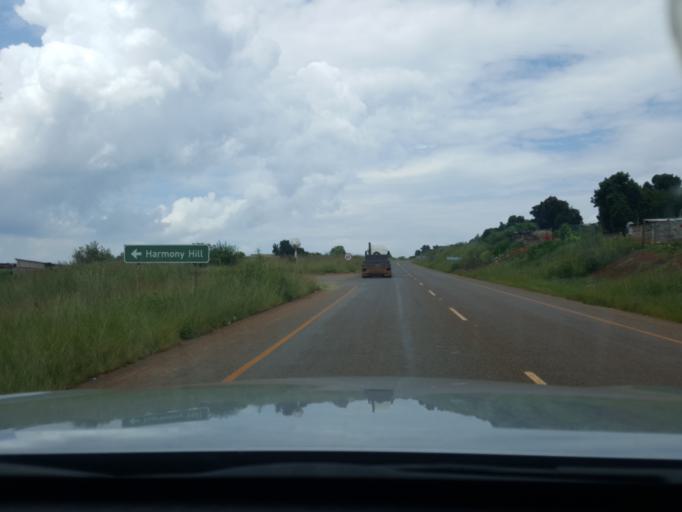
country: ZA
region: Mpumalanga
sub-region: Ehlanzeni District
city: Graksop
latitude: -25.0995
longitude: 30.7935
